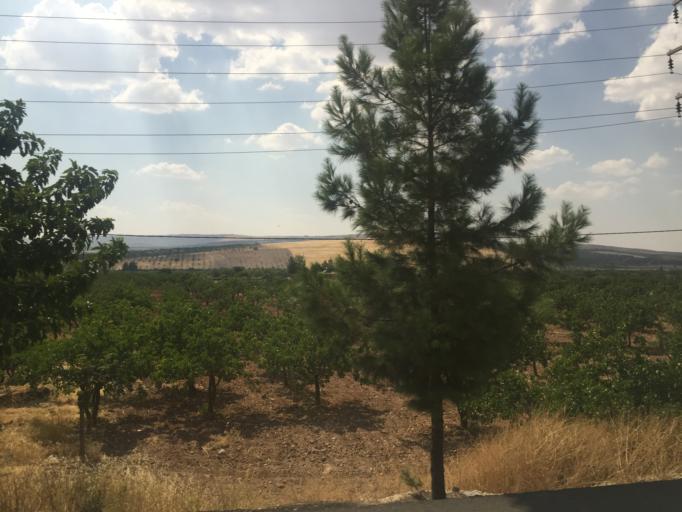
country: TR
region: Sanliurfa
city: Sanliurfa
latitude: 37.2398
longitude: 38.7939
